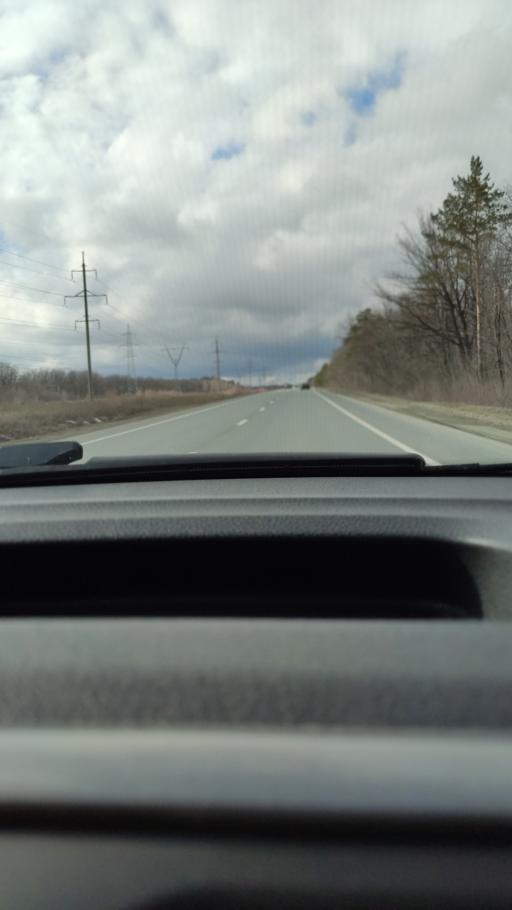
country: RU
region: Samara
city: Bogatyr'
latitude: 53.5013
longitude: 49.9505
